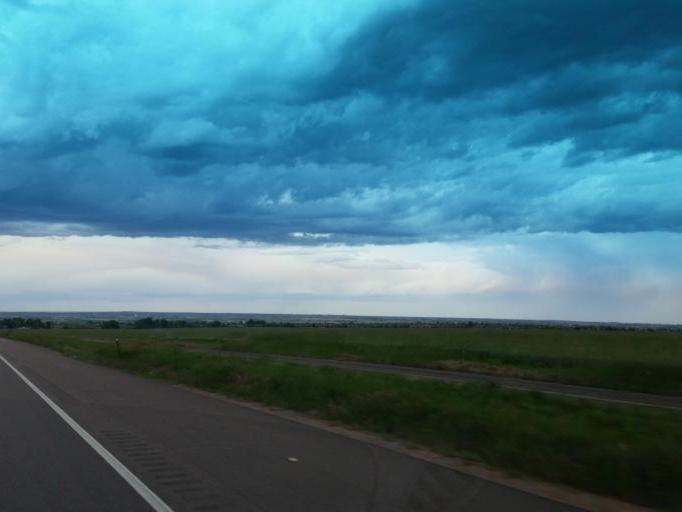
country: US
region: Colorado
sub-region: Weld County
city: Windsor
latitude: 40.4505
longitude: -104.9919
